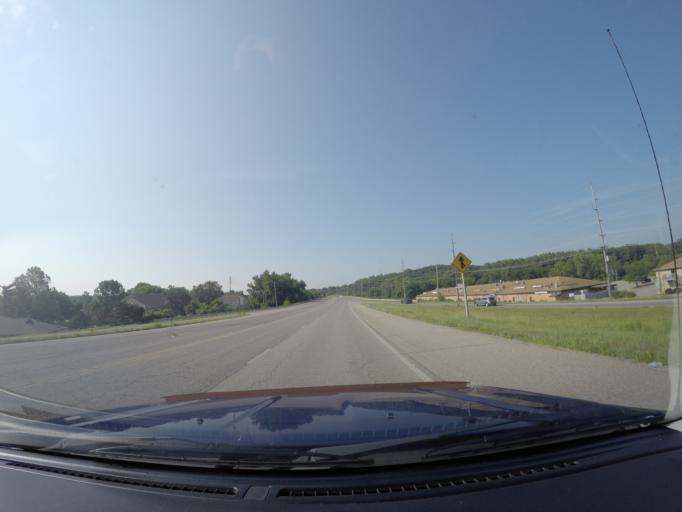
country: US
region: Kansas
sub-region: Riley County
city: Manhattan
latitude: 39.1887
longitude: -96.6116
